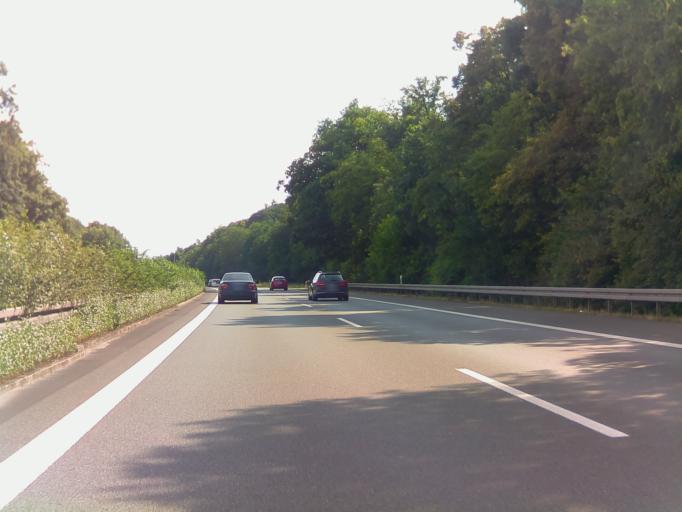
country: DE
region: Bavaria
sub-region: Regierungsbezirk Unterfranken
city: Arnstein
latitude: 49.9302
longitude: 9.9995
